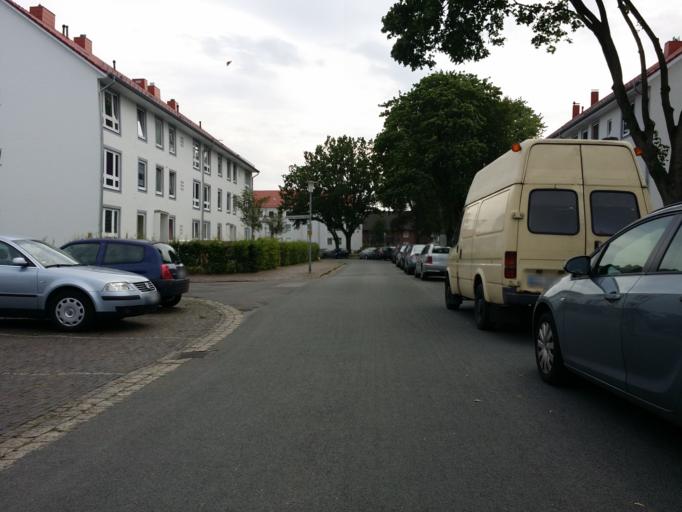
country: DE
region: Lower Saxony
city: Oldenburg
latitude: 53.1600
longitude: 8.2252
